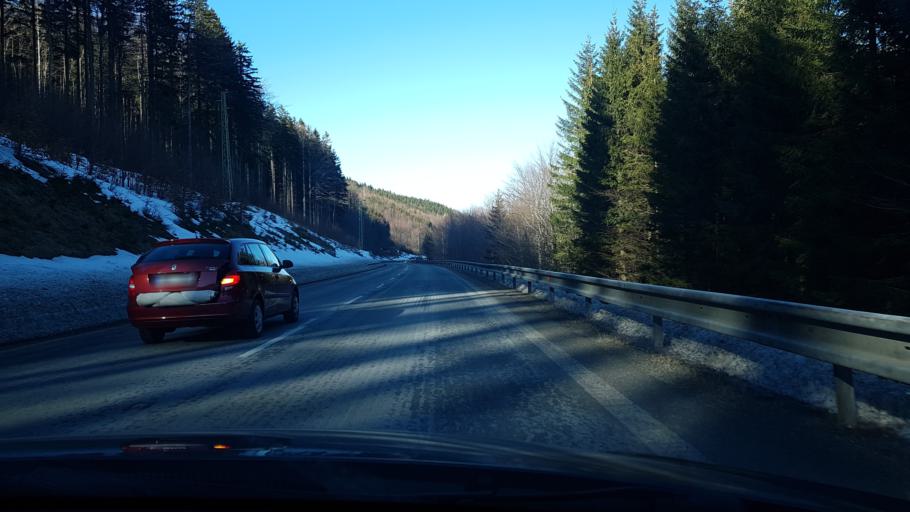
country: CZ
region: Olomoucky
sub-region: Okres Sumperk
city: Loucna nad Desnou
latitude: 50.1376
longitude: 17.1646
